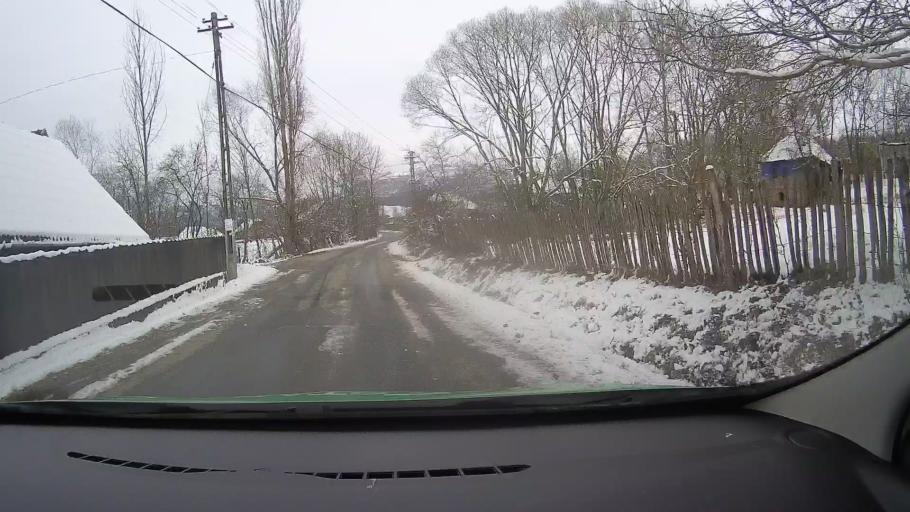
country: RO
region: Alba
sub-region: Comuna Almasu Mare
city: Almasu Mare
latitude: 46.0971
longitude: 23.1298
